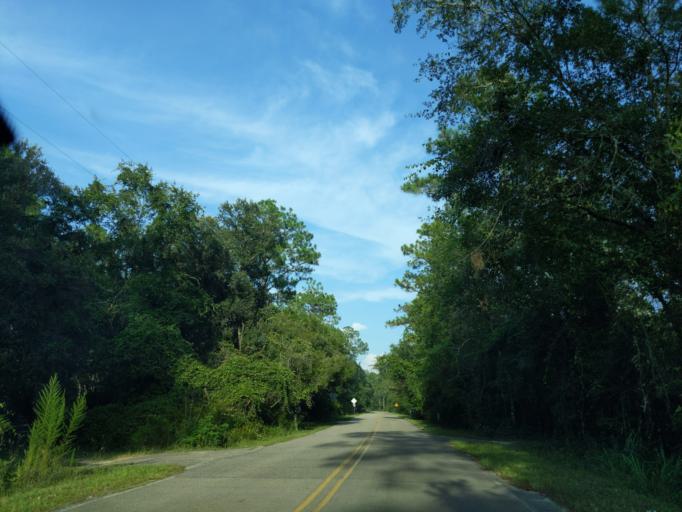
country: US
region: Florida
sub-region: Leon County
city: Tallahassee
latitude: 30.3443
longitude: -84.3915
